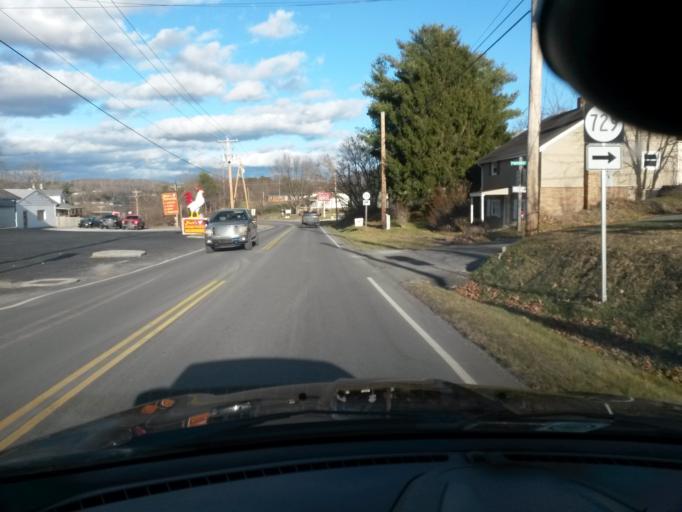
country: US
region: Virginia
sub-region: Giles County
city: Narrows
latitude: 37.3925
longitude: -80.8065
